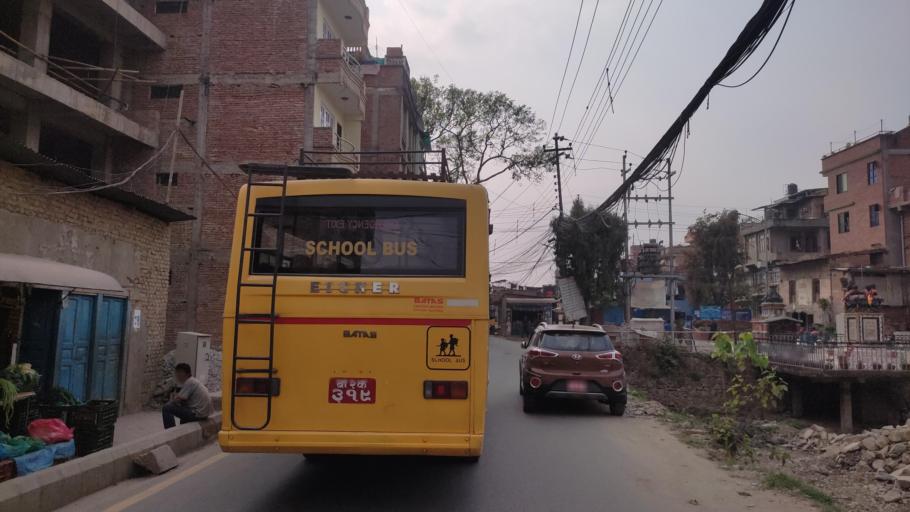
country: NP
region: Central Region
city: Kirtipur
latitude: 27.6775
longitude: 85.2755
